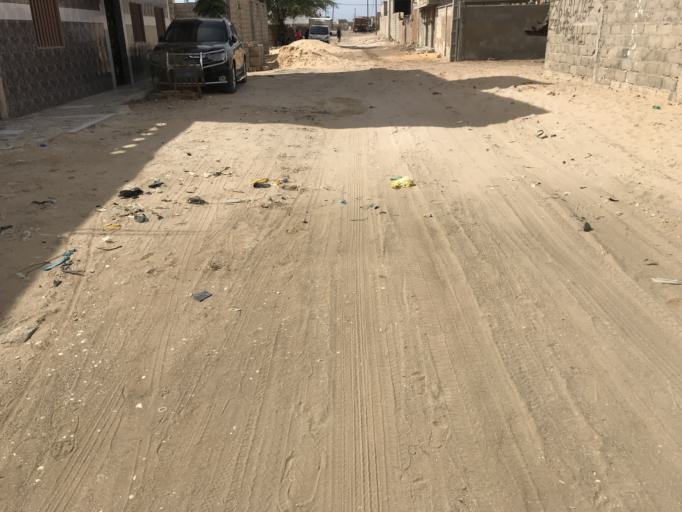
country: SN
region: Saint-Louis
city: Saint-Louis
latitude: 16.0250
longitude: -16.4809
